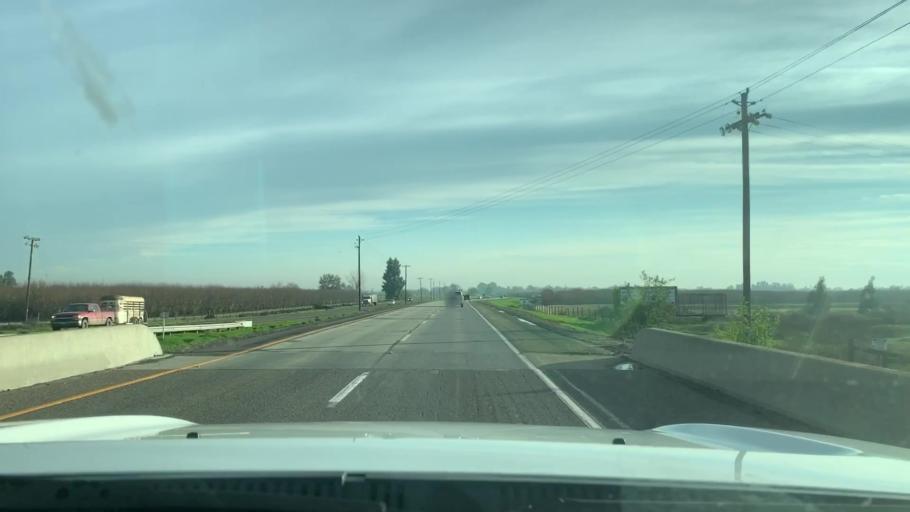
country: US
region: California
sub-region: Fresno County
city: Riverdale
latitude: 36.3858
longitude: -119.8098
